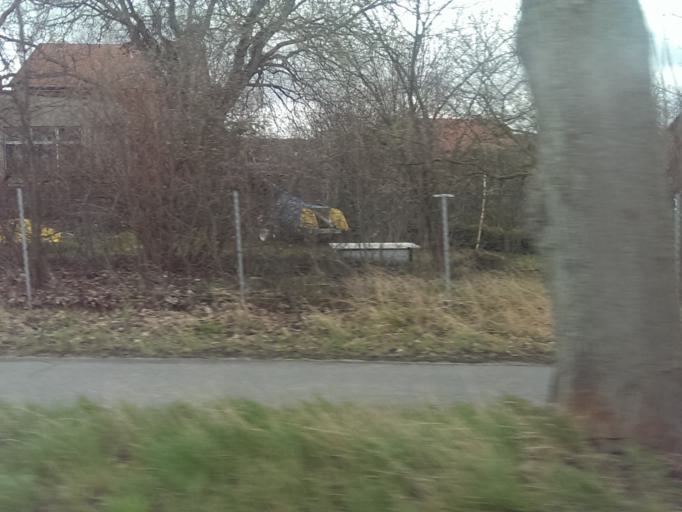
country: DE
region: Lower Saxony
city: Hildesheim
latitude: 52.1398
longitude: 10.0226
